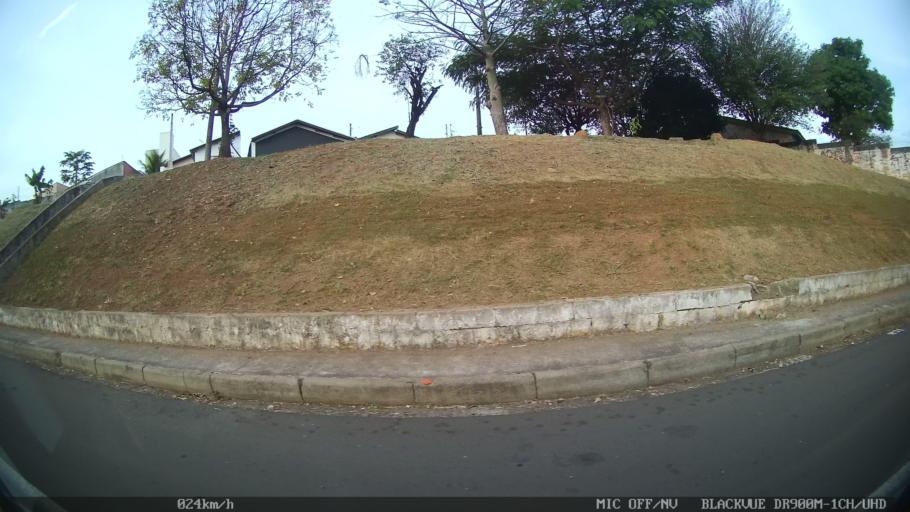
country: BR
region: Sao Paulo
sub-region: Limeira
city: Limeira
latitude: -22.5777
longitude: -47.4130
